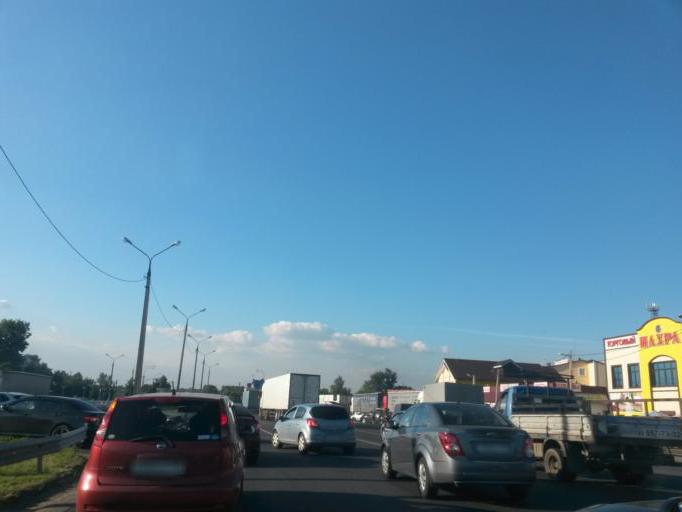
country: RU
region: Moskovskaya
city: Yam
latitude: 55.4878
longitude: 37.7499
